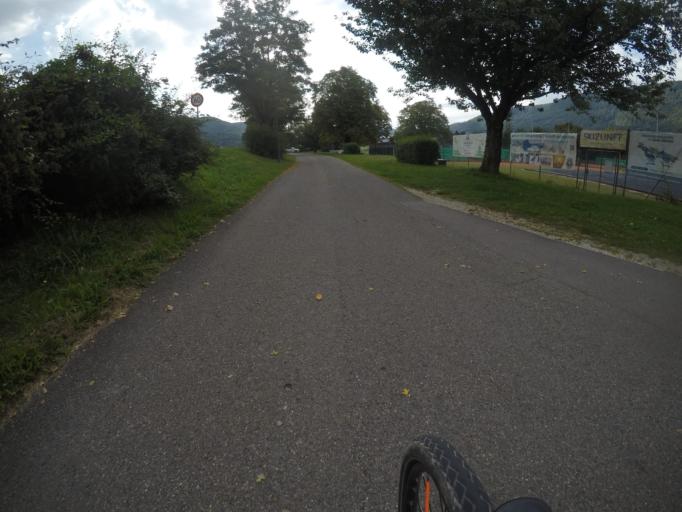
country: DE
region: Baden-Wuerttemberg
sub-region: Tuebingen Region
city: Dettingen an der Erms
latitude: 48.5235
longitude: 9.3559
